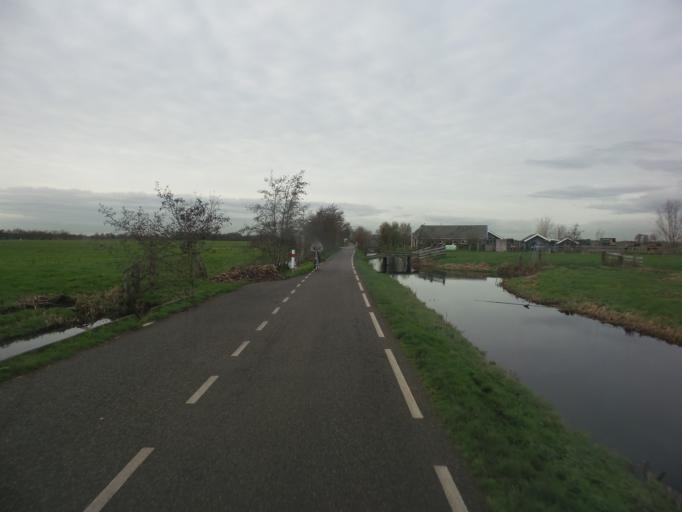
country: NL
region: South Holland
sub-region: Gemeente Vlist
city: Haastrecht
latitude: 52.0240
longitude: 4.7877
